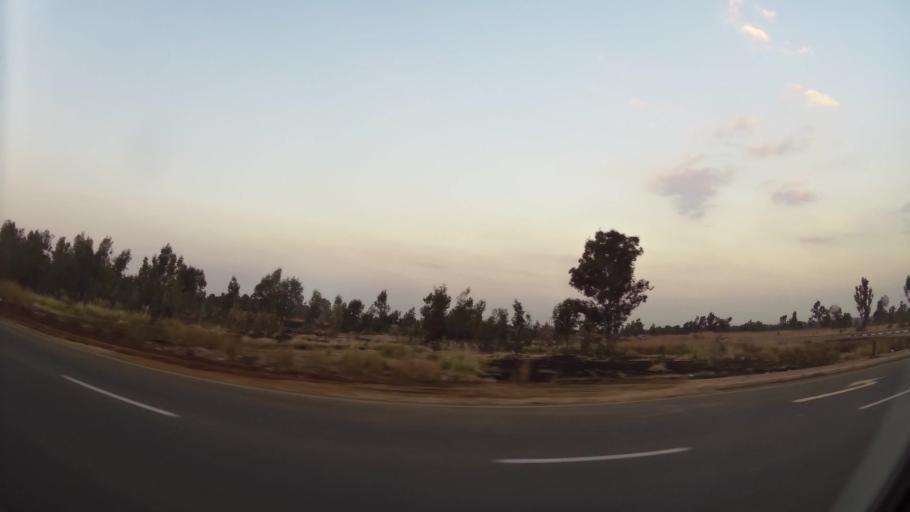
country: ZA
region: Gauteng
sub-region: Ekurhuleni Metropolitan Municipality
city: Springs
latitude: -26.2768
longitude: 28.4295
